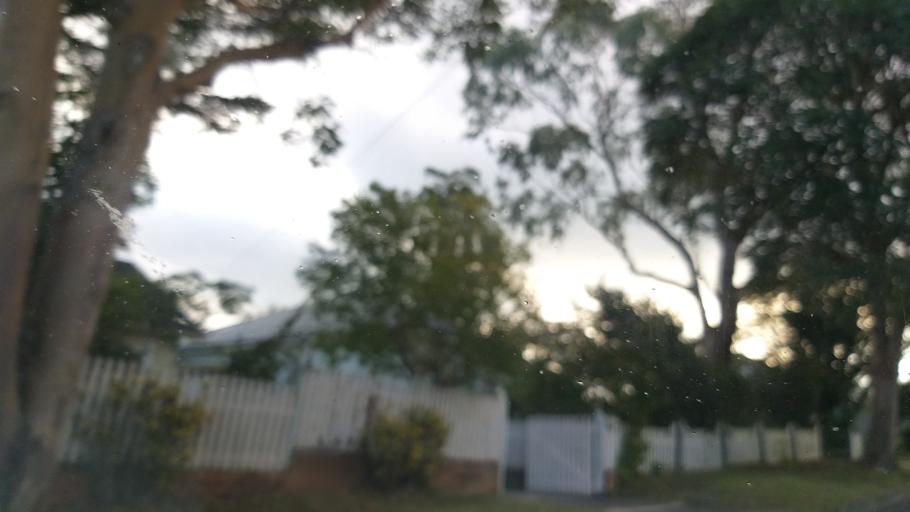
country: AU
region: New South Wales
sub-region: Wollongong
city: West Wollongong
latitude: -34.4241
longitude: 150.8633
